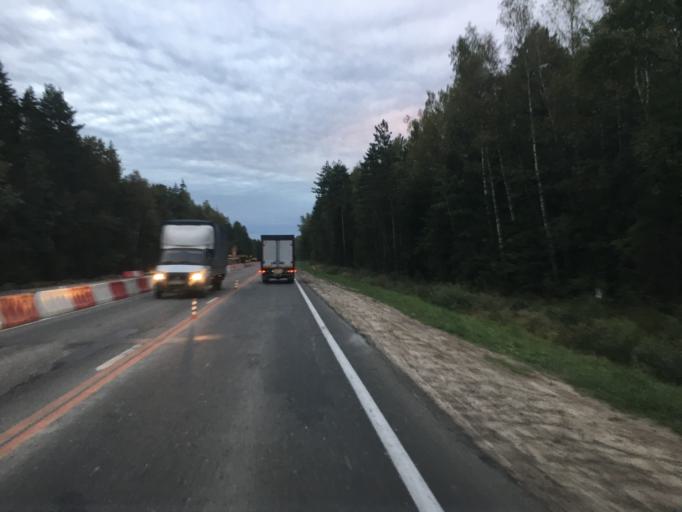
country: RU
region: Kaluga
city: Detchino
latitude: 54.7116
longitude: 36.2903
